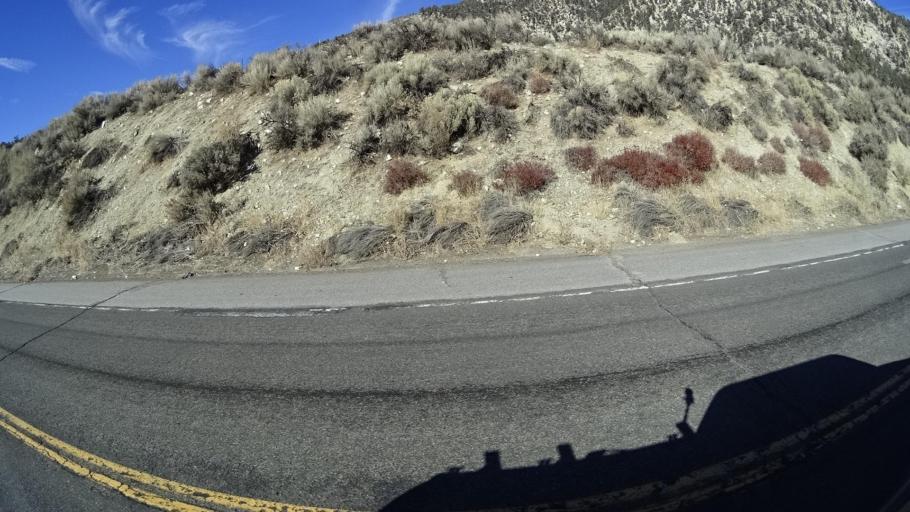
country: US
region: California
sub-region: Kern County
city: Frazier Park
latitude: 34.8191
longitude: -118.9901
